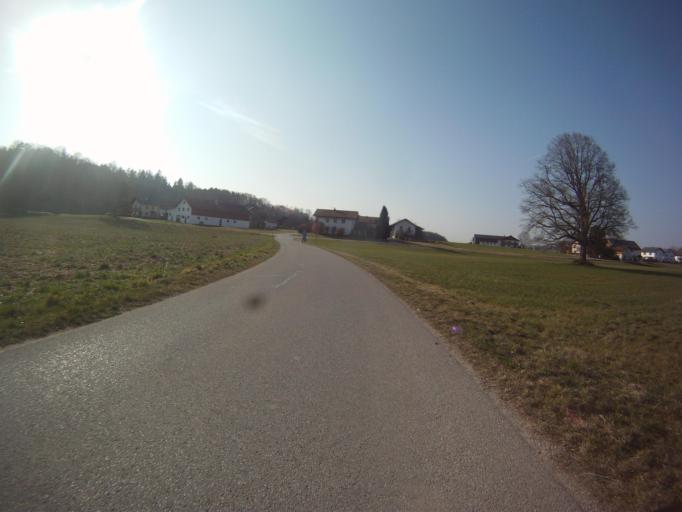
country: DE
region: Bavaria
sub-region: Upper Bavaria
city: Haiming
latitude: 48.2217
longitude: 12.8765
